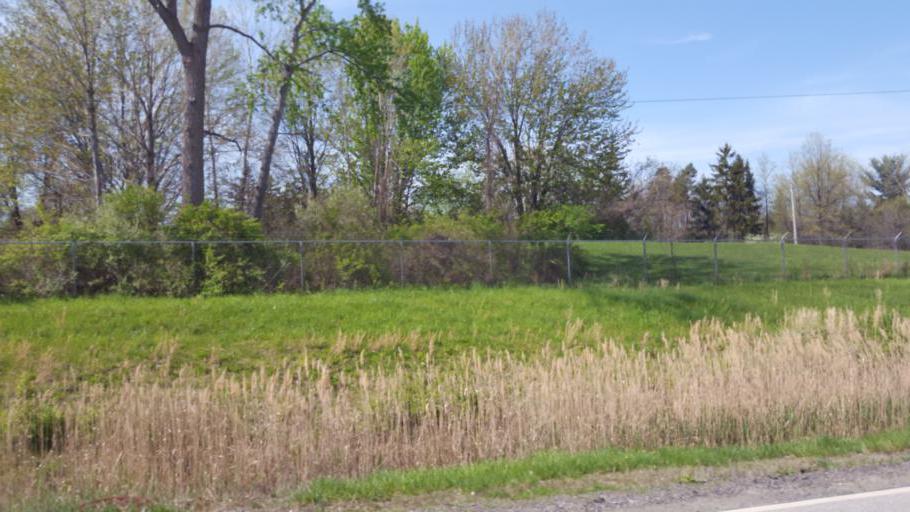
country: US
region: Ohio
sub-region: Lake County
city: Fairport Harbor
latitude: 41.7257
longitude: -81.2714
